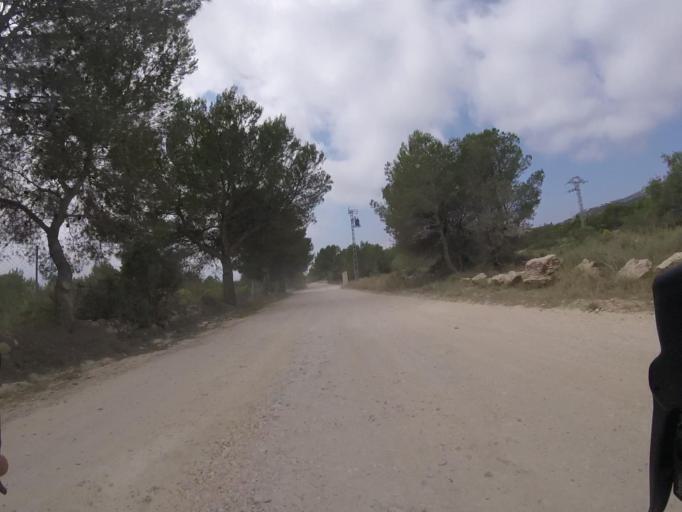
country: ES
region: Valencia
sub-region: Provincia de Castello
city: Alcoceber
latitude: 40.2611
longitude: 0.2978
